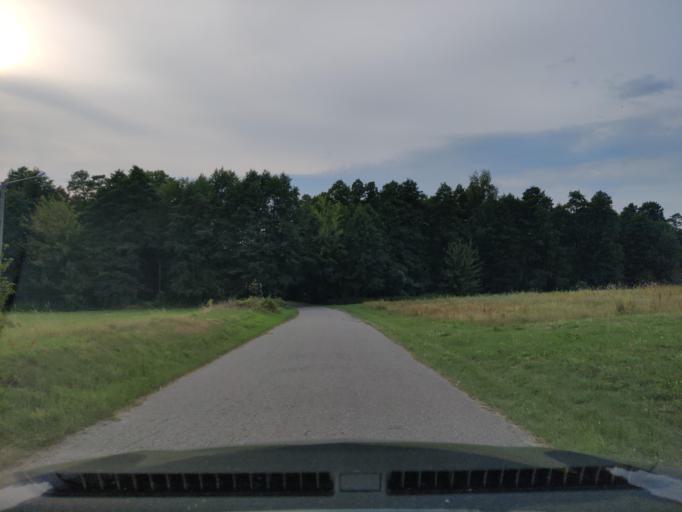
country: PL
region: Masovian Voivodeship
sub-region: Powiat pultuski
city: Obryte
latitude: 52.7415
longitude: 21.2508
